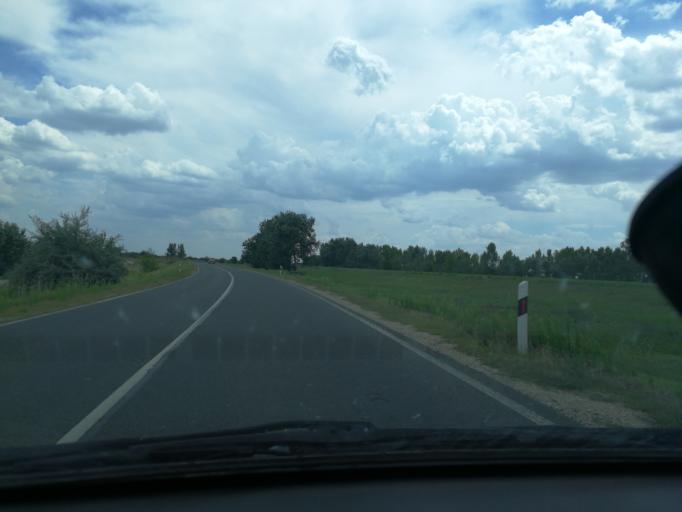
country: HU
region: Bacs-Kiskun
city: Harta
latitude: 46.7341
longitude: 19.0133
